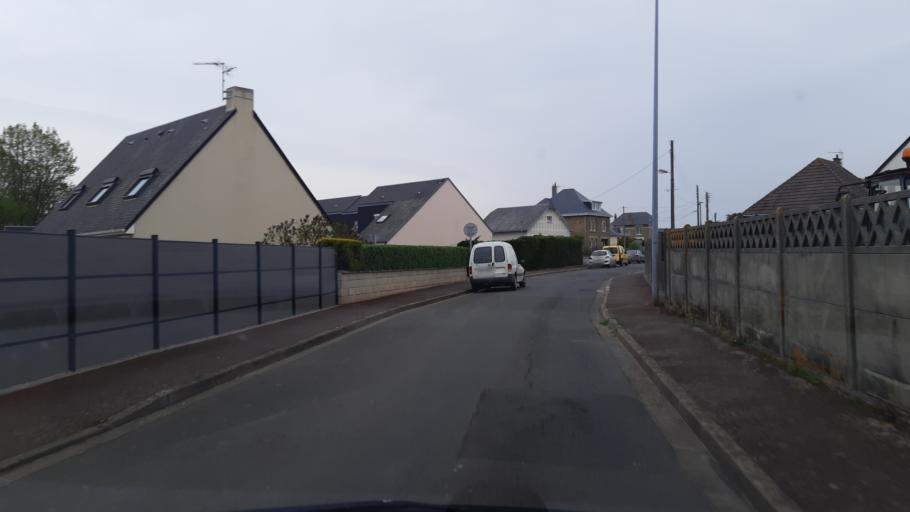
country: FR
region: Lower Normandy
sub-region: Departement de la Manche
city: Donville-les-Bains
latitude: 48.8389
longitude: -1.5796
